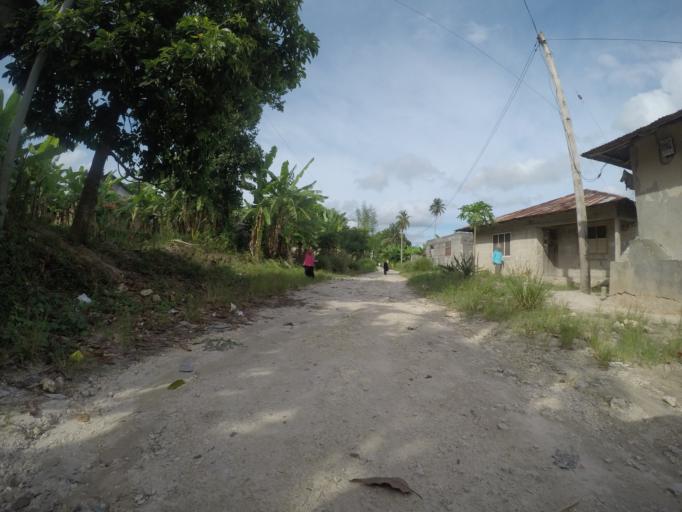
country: TZ
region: Pemba South
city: Chake Chake
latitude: -5.2255
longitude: 39.7775
